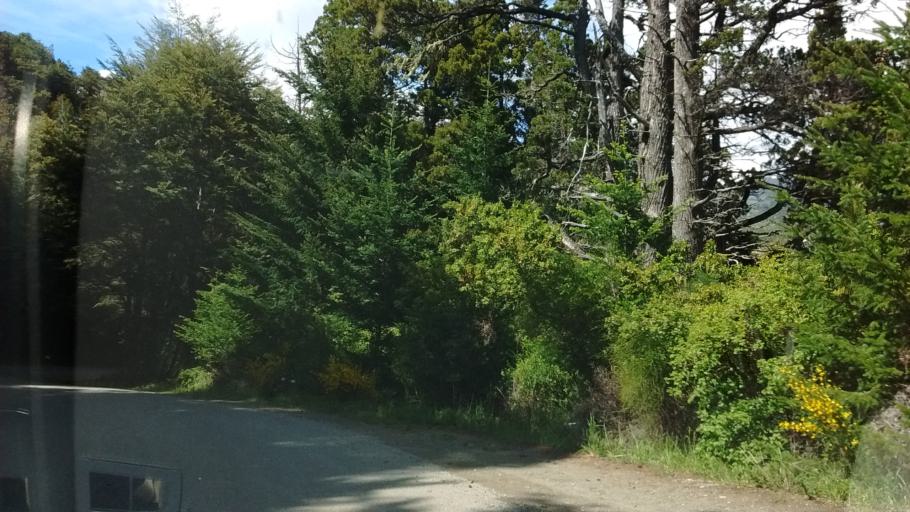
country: AR
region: Rio Negro
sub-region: Departamento de Bariloche
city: San Carlos de Bariloche
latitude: -41.0727
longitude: -71.5450
